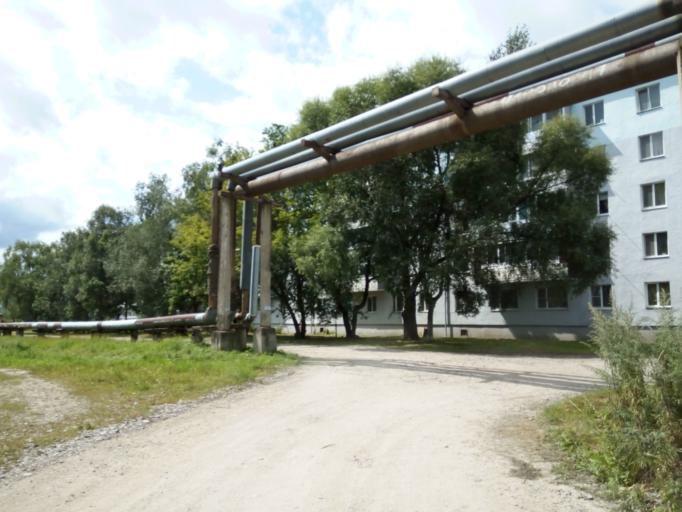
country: RU
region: Primorskiy
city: Dal'nerechensk
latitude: 45.9437
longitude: 133.8165
